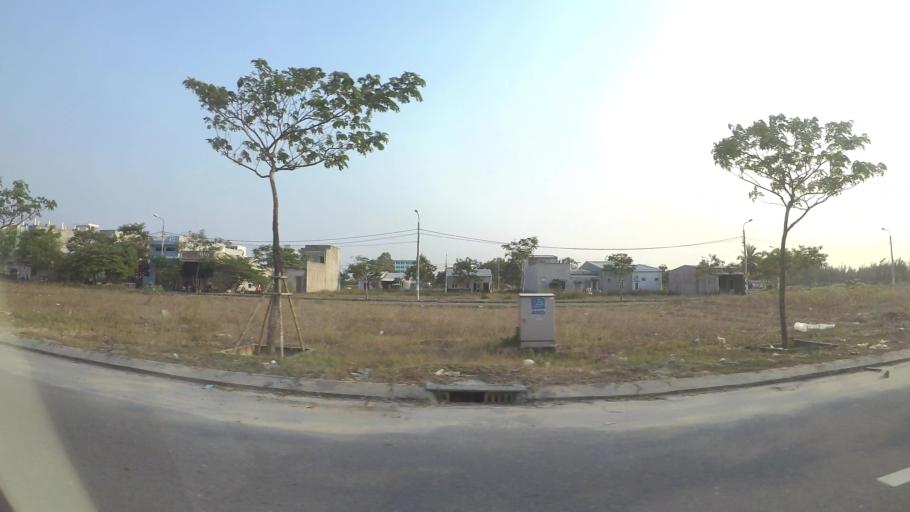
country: VN
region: Da Nang
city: Ngu Hanh Son
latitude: 15.9831
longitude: 108.2478
